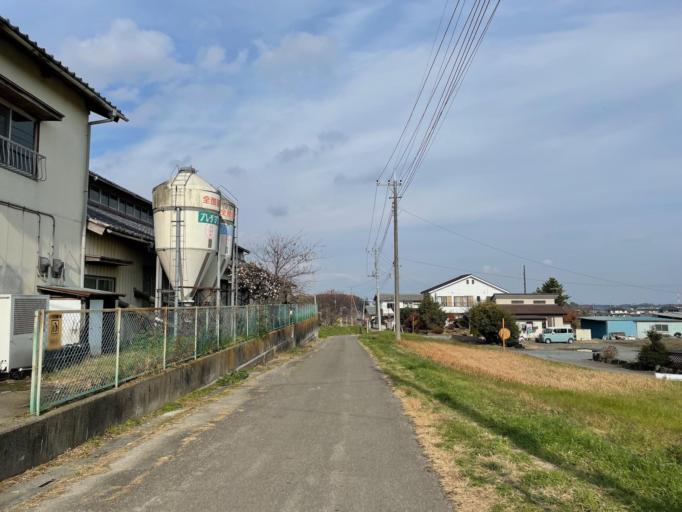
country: JP
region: Saitama
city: Yorii
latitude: 36.1496
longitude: 139.1946
